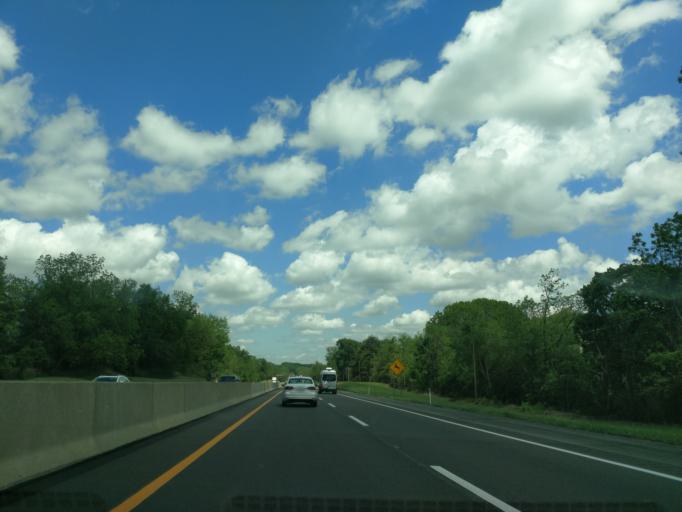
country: US
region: Pennsylvania
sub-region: Chester County
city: Chesterbrook
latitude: 40.0778
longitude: -75.4744
